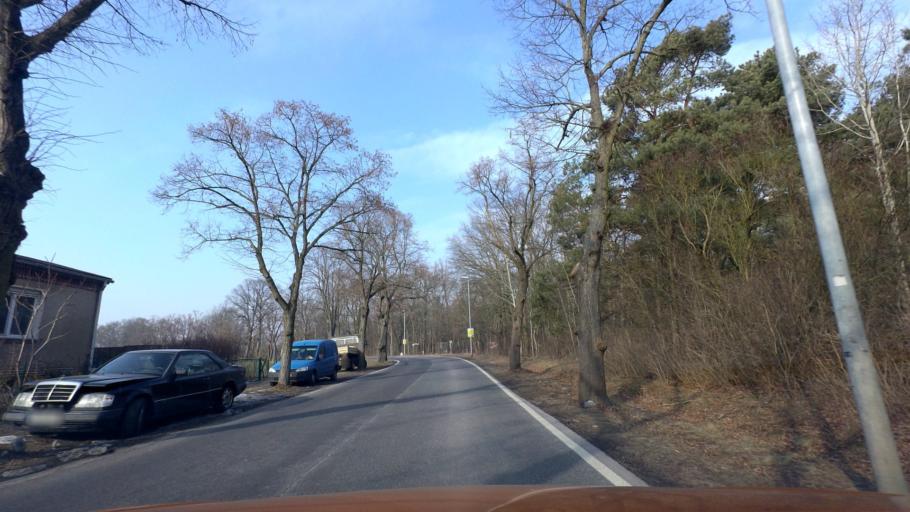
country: DE
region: Brandenburg
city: Am Mellensee
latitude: 52.1862
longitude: 13.4001
